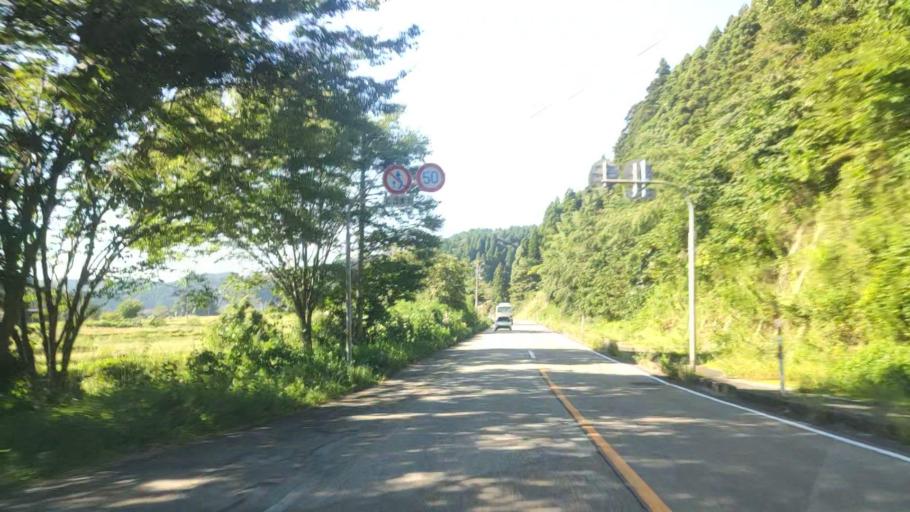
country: JP
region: Ishikawa
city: Nanao
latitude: 37.2748
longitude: 137.0542
